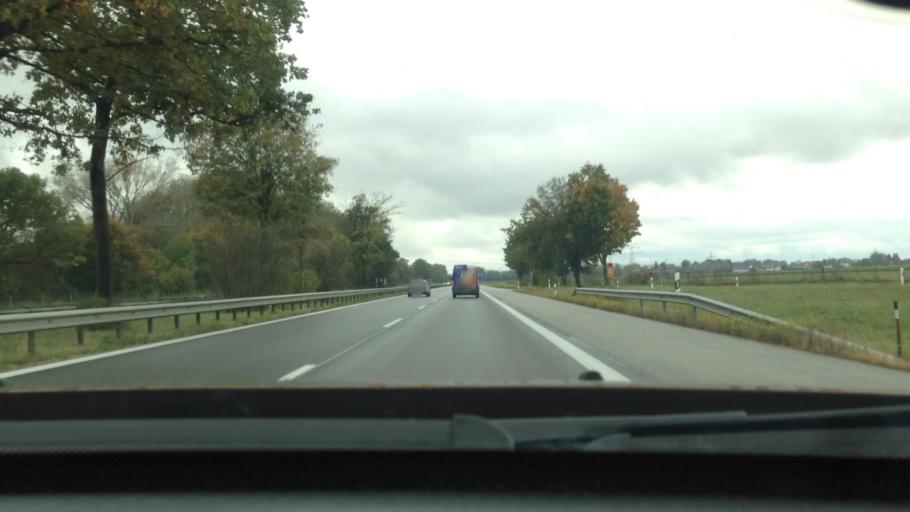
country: DE
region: Bavaria
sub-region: Upper Bavaria
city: Grobenzell
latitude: 48.1952
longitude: 11.4113
